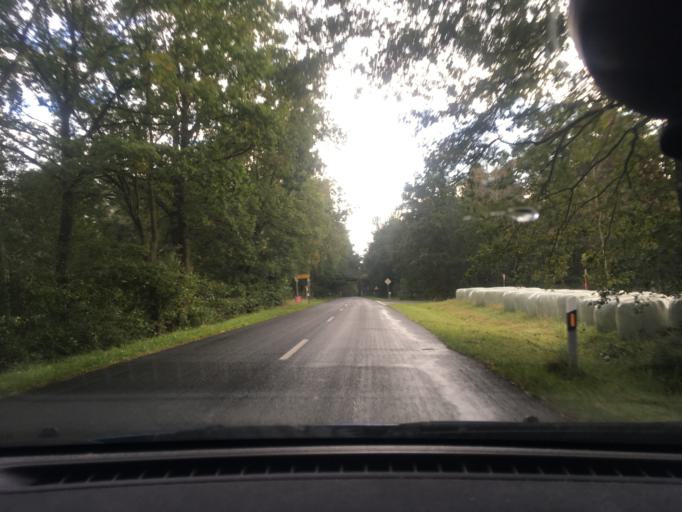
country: DE
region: Lower Saxony
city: Gohrde
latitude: 53.1721
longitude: 10.8729
